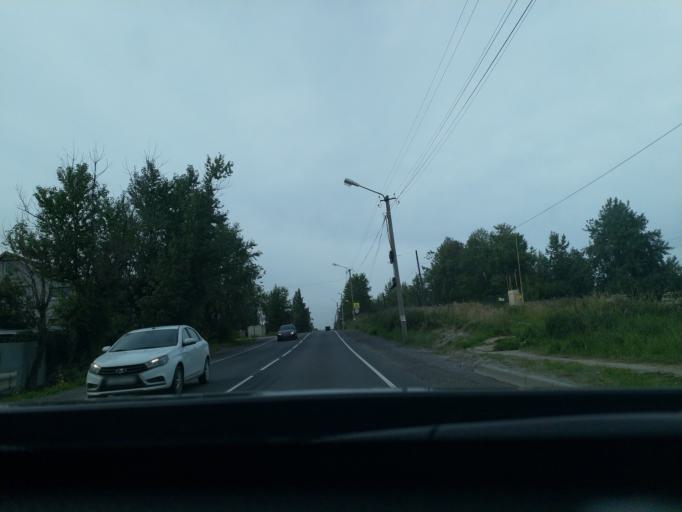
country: RU
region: Leningrad
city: Nikol'skoye
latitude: 59.7147
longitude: 30.7794
